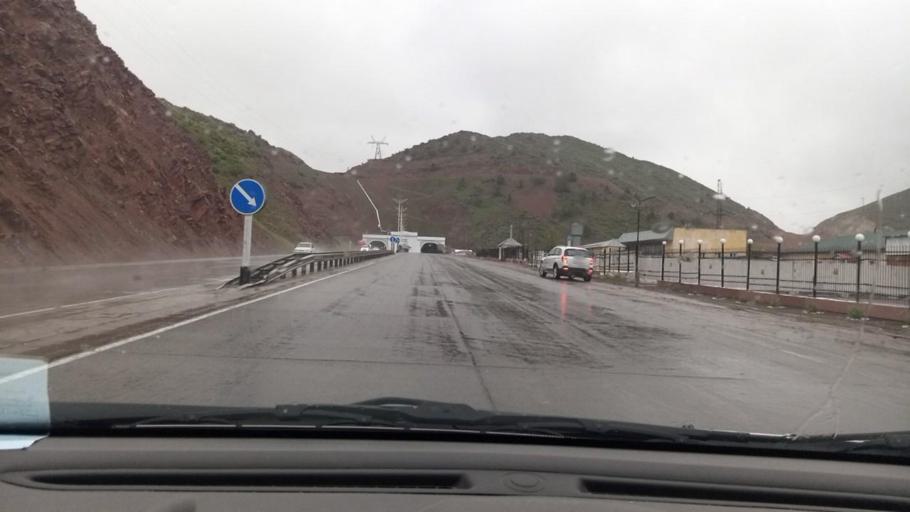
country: UZ
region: Toshkent
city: Angren
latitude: 41.0822
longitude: 70.5439
